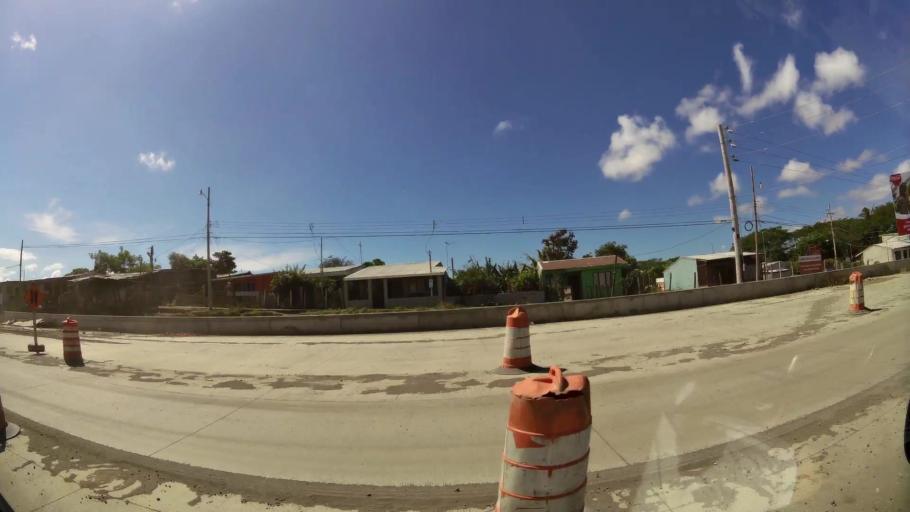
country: CR
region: Guanacaste
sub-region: Canton de Canas
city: Canas
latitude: 10.4226
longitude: -85.0910
